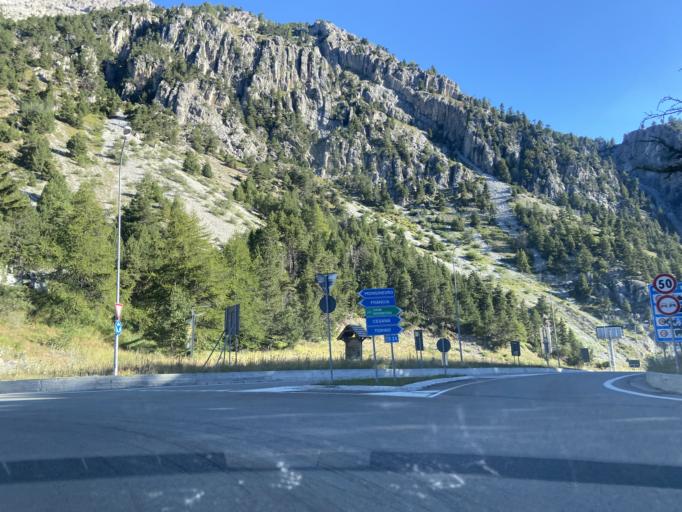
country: IT
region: Piedmont
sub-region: Provincia di Torino
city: Claviere
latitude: 44.9420
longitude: 6.7583
